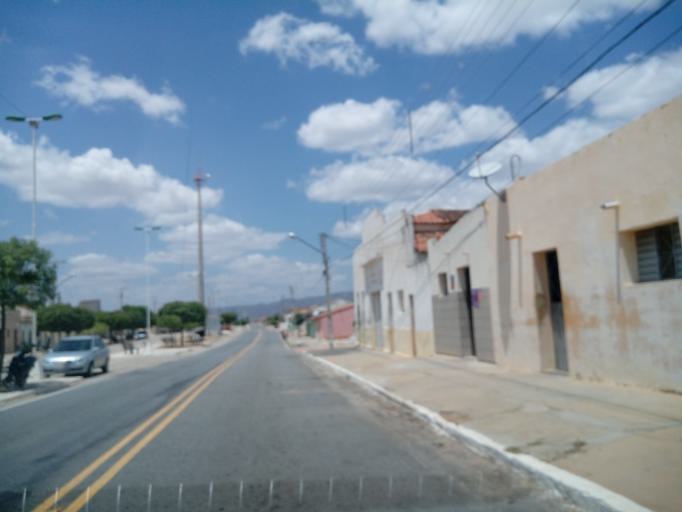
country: BR
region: Paraiba
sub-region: Desterro
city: Desterro
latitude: -7.1180
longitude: -37.0683
